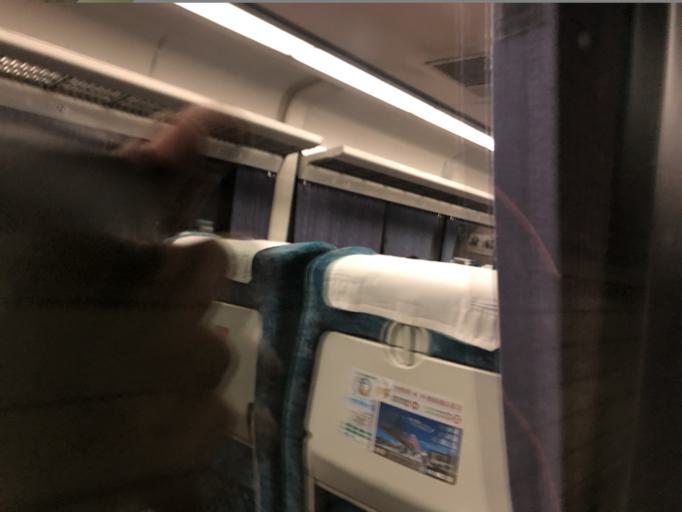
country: JP
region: Kochi
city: Nakamura
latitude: 33.0912
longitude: 133.1017
